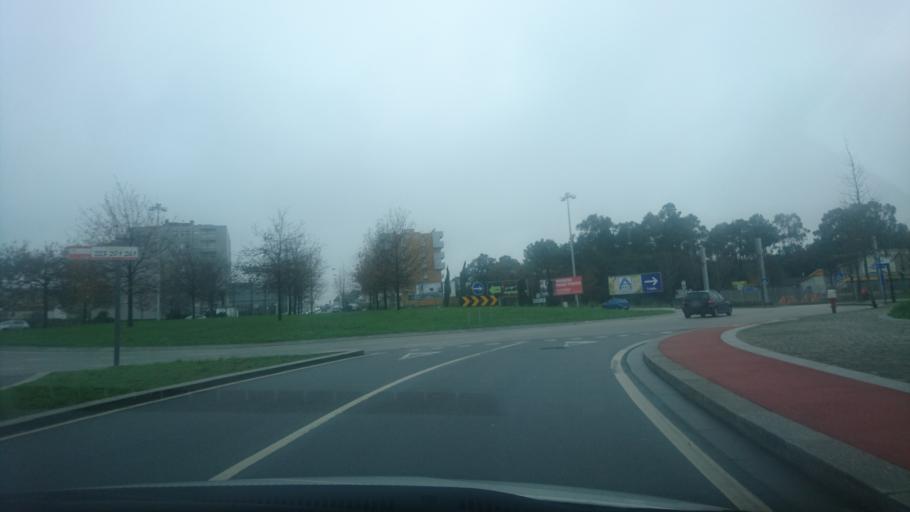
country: PT
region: Porto
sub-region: Gondomar
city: Fanzeres
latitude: 41.1685
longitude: -8.5428
